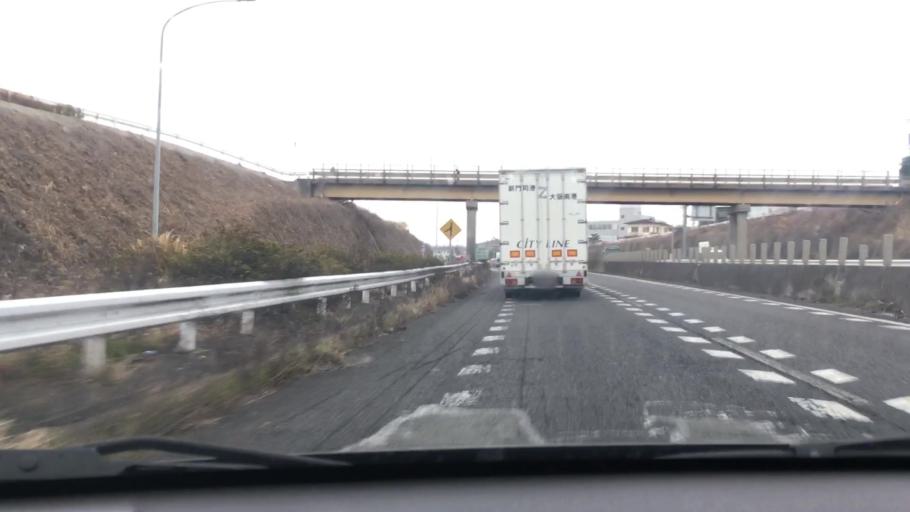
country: JP
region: Mie
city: Ueno-ebisumachi
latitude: 34.7551
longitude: 136.1475
